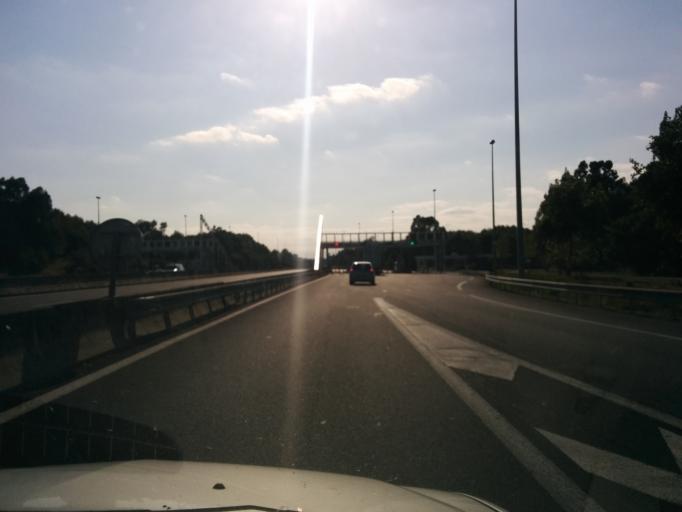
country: FR
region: Pays de la Loire
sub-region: Departement de la Loire-Atlantique
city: Carquefou
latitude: 47.2914
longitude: -1.4786
